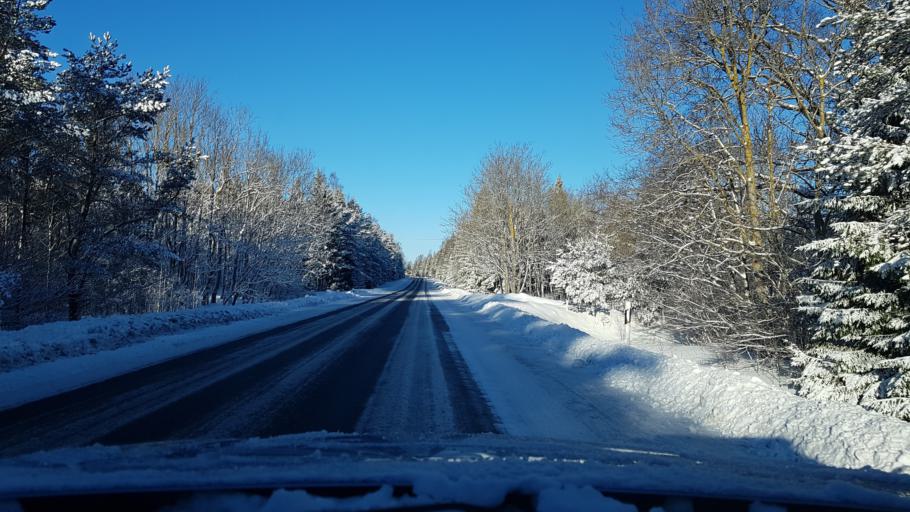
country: EE
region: Hiiumaa
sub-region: Kaerdla linn
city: Kardla
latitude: 58.9724
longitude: 22.8236
